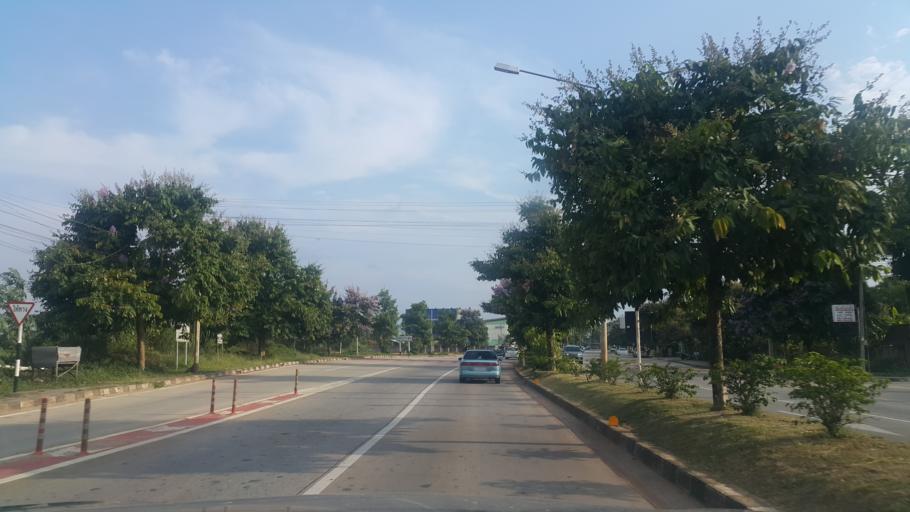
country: TH
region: Chiang Rai
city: Chiang Rai
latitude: 19.9225
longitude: 99.8620
